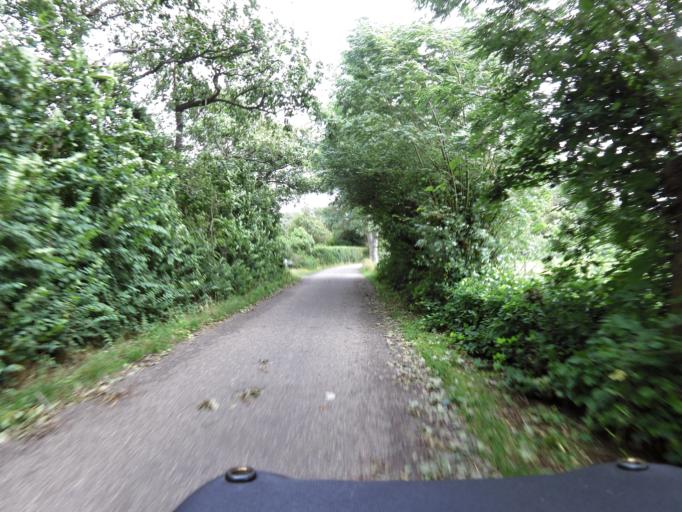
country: NL
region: South Holland
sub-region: Gemeente Goeree-Overflakkee
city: Goedereede
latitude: 51.8357
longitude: 3.9838
